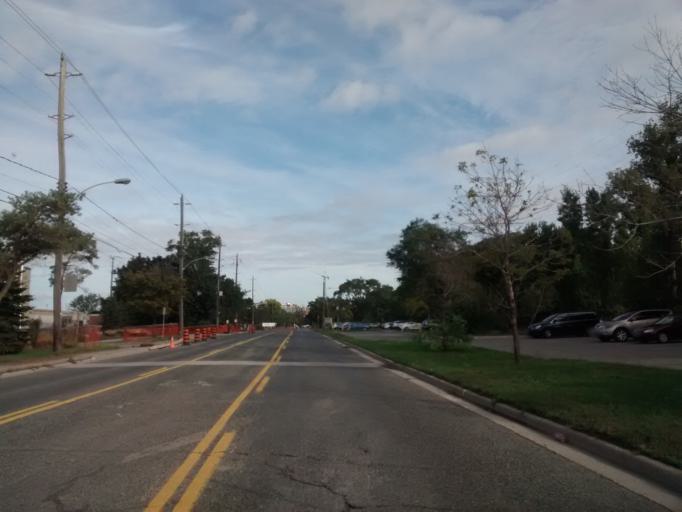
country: CA
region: Ontario
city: Hamilton
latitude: 43.3075
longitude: -79.8001
